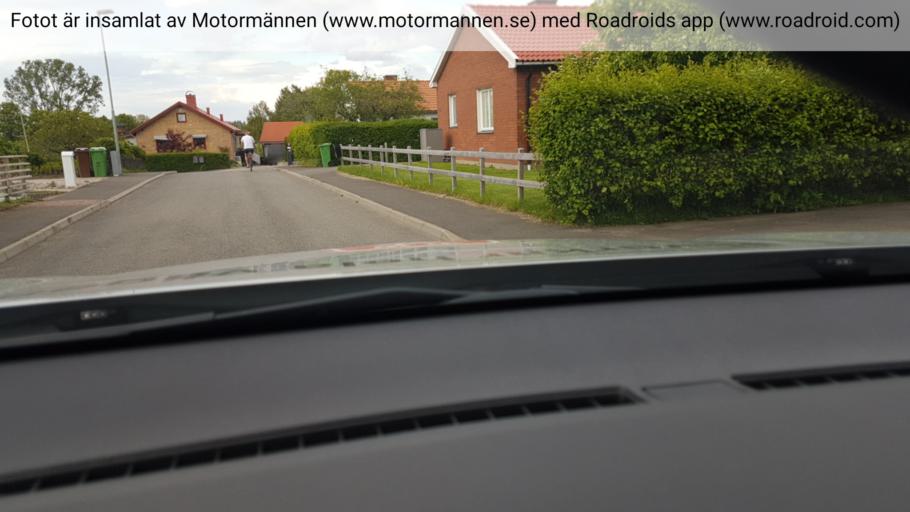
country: SE
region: Vaestra Goetaland
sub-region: Skovde Kommun
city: Skoevde
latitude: 58.3852
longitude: 13.8719
